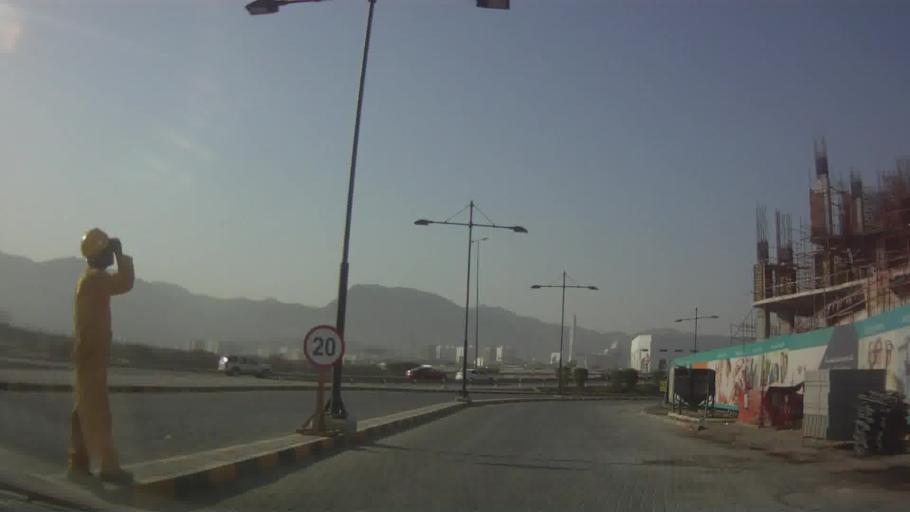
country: OM
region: Muhafazat Masqat
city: Bawshar
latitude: 23.5903
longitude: 58.4138
